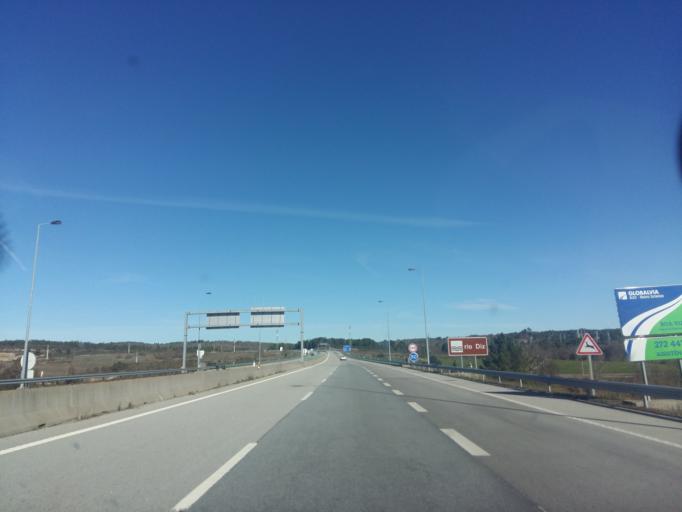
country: PT
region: Guarda
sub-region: Guarda
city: Sequeira
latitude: 40.5261
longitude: -7.2233
